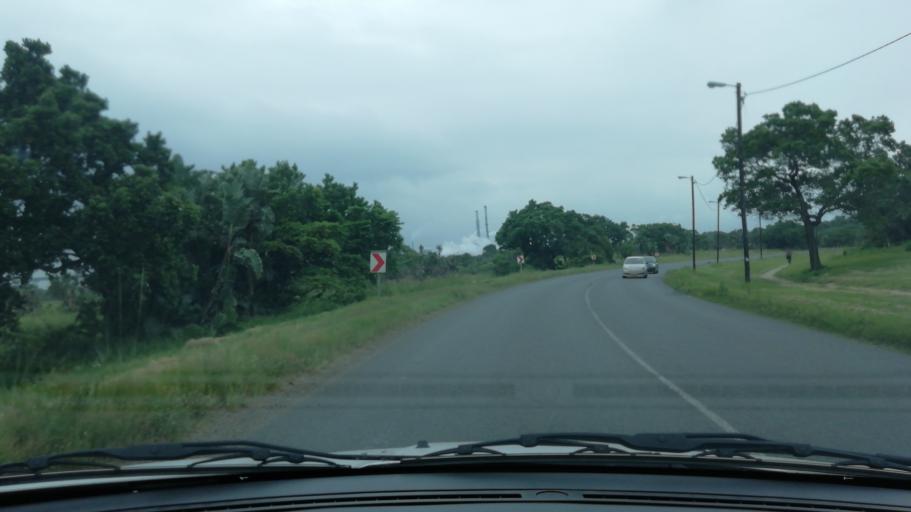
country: ZA
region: KwaZulu-Natal
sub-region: uThungulu District Municipality
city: Richards Bay
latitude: -28.7617
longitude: 32.0428
